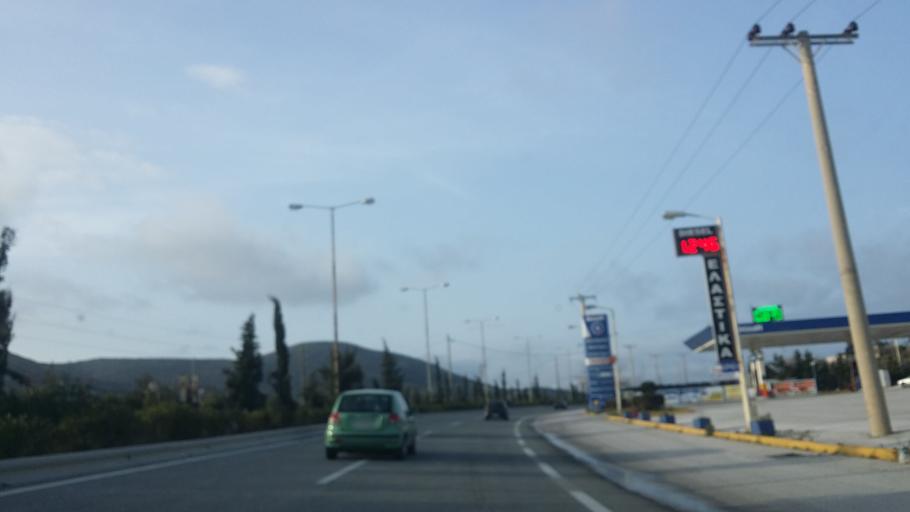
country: GR
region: Attica
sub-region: Nomarchia Anatolikis Attikis
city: Lavrio
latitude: 37.7710
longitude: 24.0541
